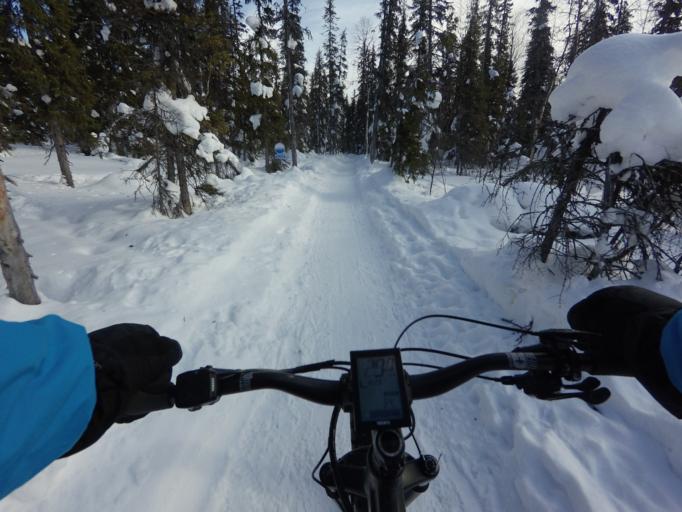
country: FI
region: Lapland
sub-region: Tunturi-Lappi
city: Kolari
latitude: 67.6031
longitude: 24.2249
